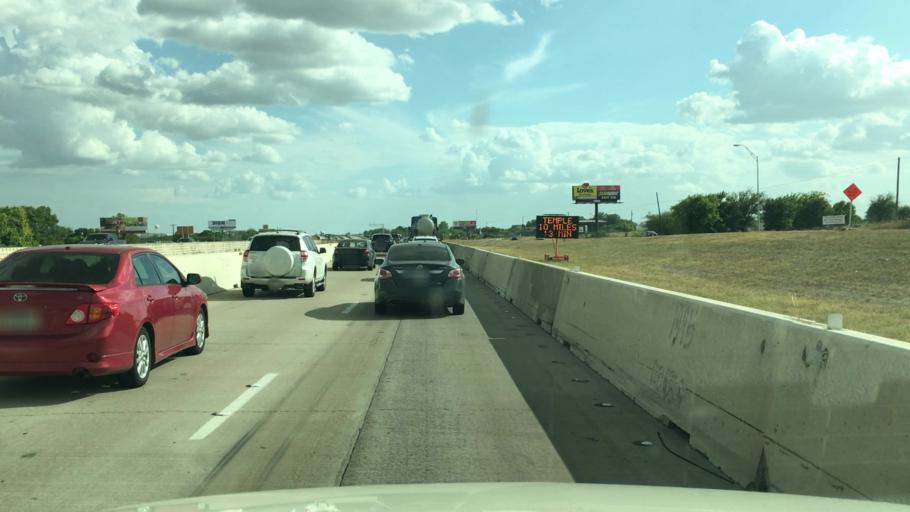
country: US
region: Texas
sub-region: Bell County
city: Troy
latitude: 31.2136
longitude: -97.3004
